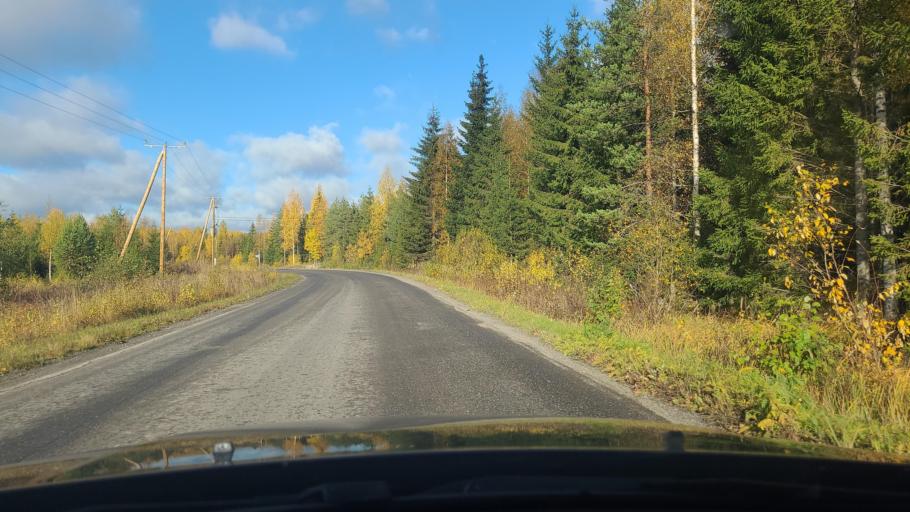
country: FI
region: Southern Savonia
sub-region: Pieksaemaeki
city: Juva
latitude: 61.8818
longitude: 27.7558
